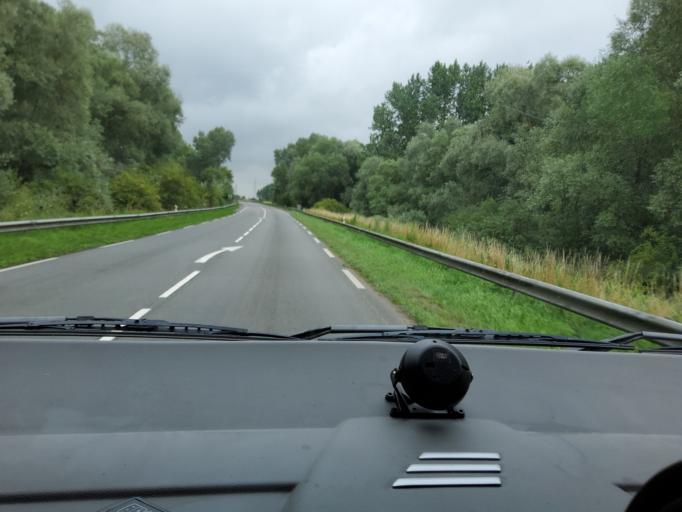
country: FR
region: Nord-Pas-de-Calais
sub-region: Departement du Nord
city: Watten
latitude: 50.8382
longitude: 2.2040
